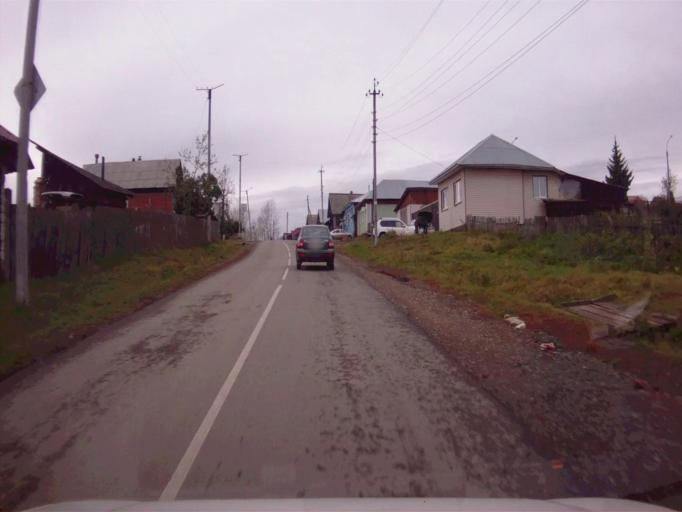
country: RU
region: Chelyabinsk
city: Nyazepetrovsk
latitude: 56.0576
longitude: 59.5860
